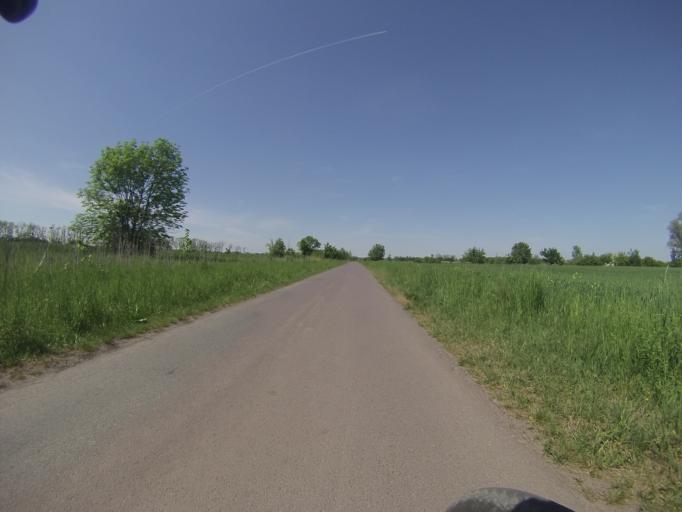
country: CZ
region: South Moravian
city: Novosedly
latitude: 48.8054
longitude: 16.4870
